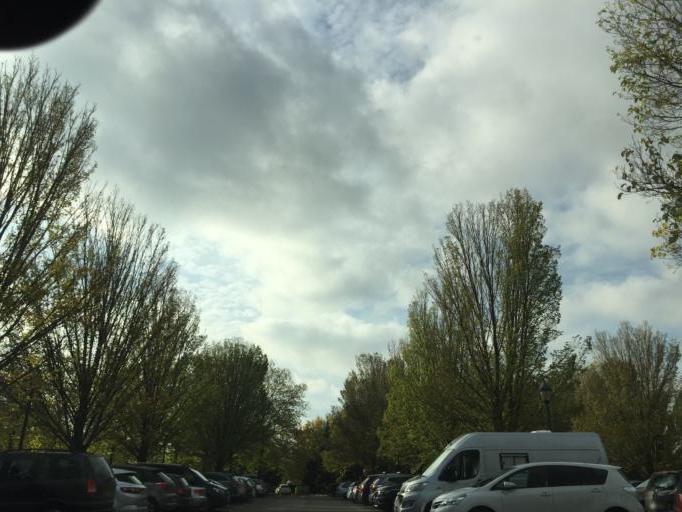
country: FR
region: Ile-de-France
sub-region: Departement de Seine-et-Marne
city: Chalifert
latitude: 48.8713
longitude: 2.7874
